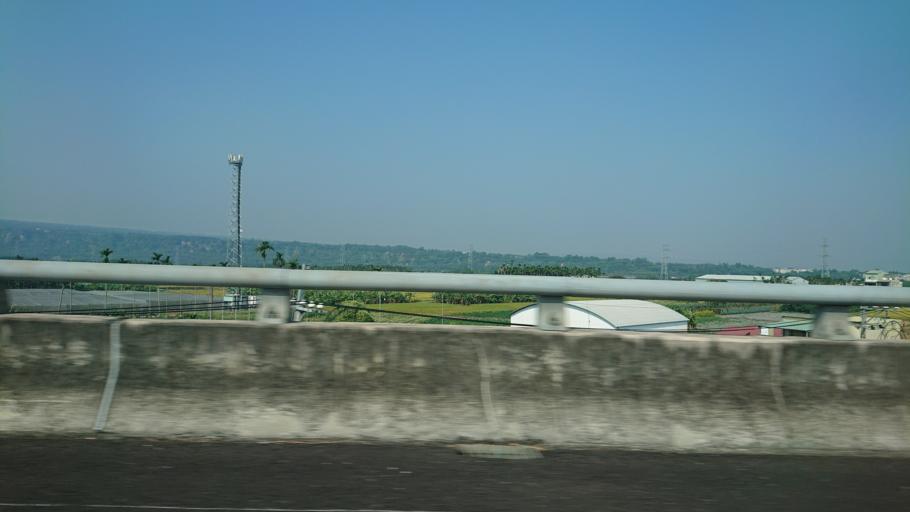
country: TW
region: Taiwan
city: Lugu
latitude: 23.8203
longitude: 120.7052
